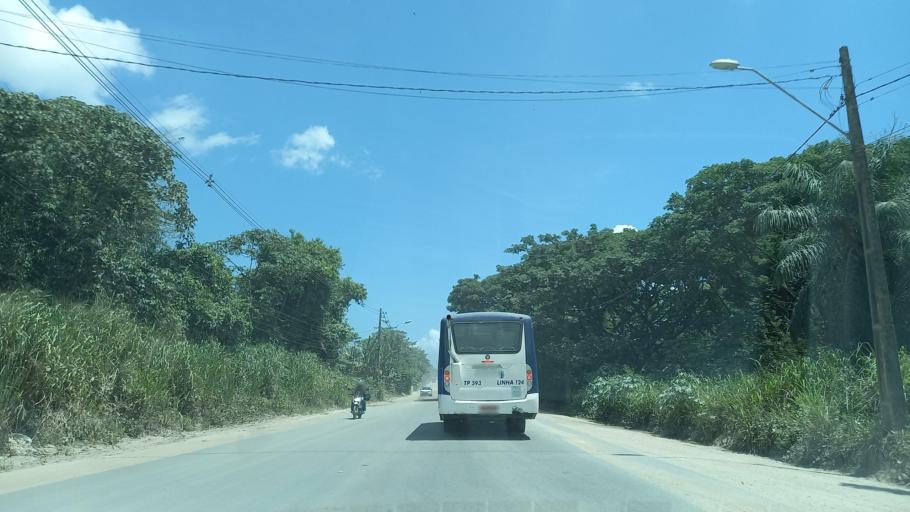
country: BR
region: Pernambuco
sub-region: Jaboatao Dos Guararapes
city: Jaboatao
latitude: -8.1597
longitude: -34.9812
